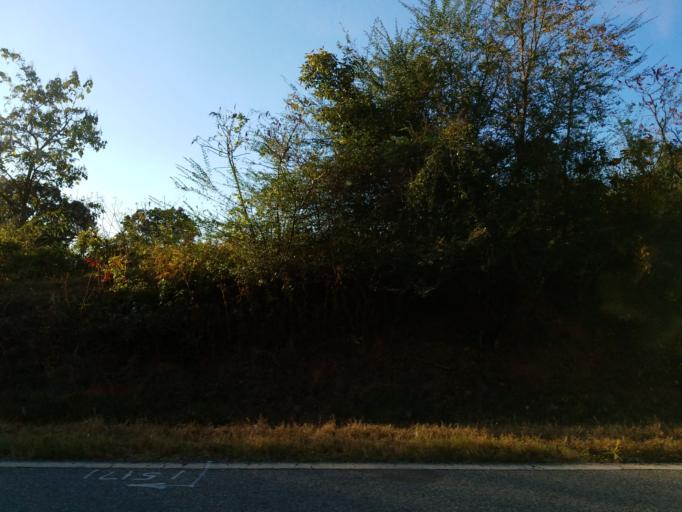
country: US
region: Georgia
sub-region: Dawson County
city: Dawsonville
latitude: 34.5419
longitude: -84.1650
